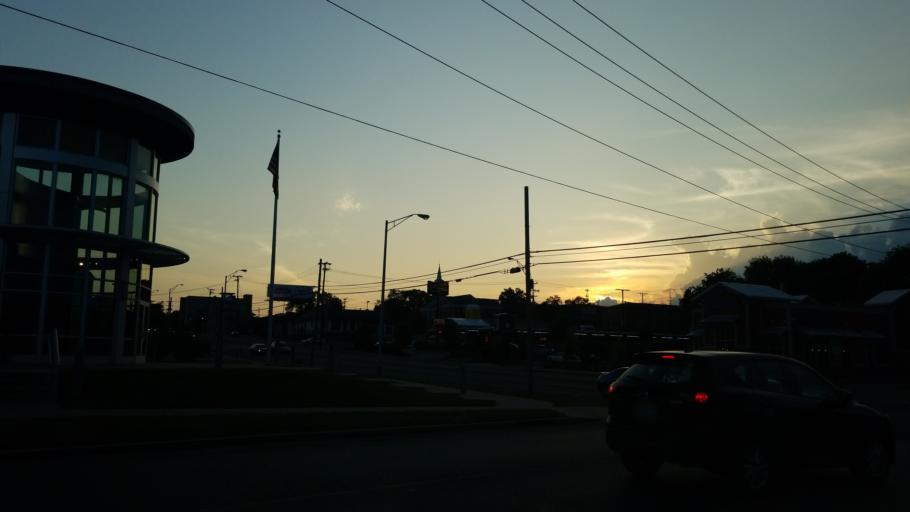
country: US
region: Tennessee
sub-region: Davidson County
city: Nashville
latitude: 36.1574
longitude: -86.8012
